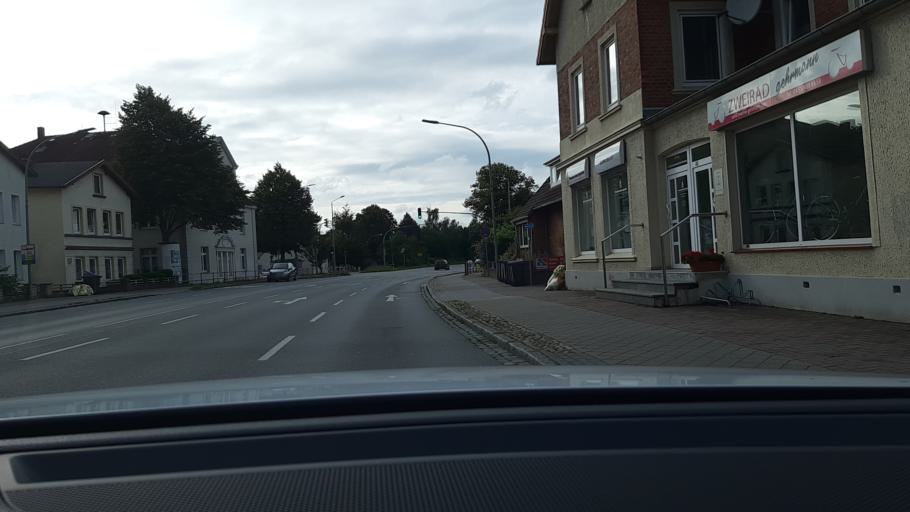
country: DE
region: Schleswig-Holstein
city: Stockelsdorf
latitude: 53.8884
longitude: 10.6425
